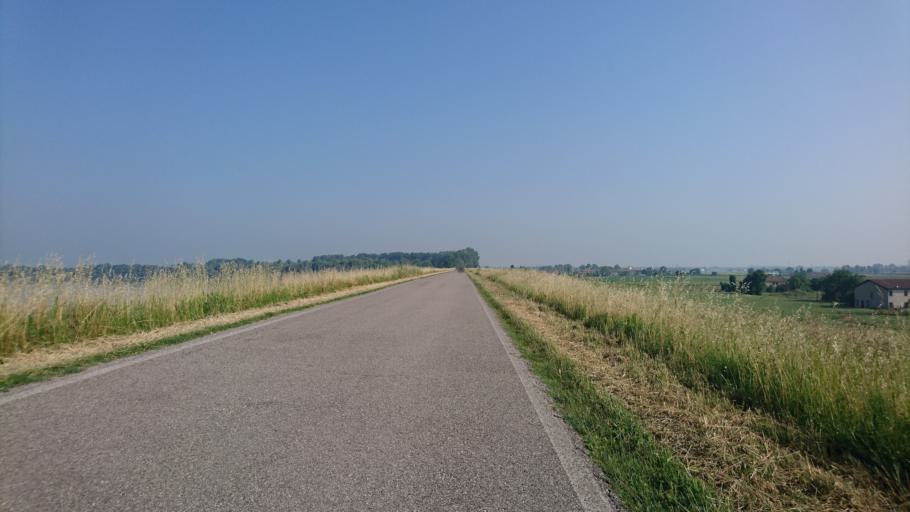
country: IT
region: Veneto
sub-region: Provincia di Rovigo
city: Bergantino
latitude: 45.0506
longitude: 11.2724
